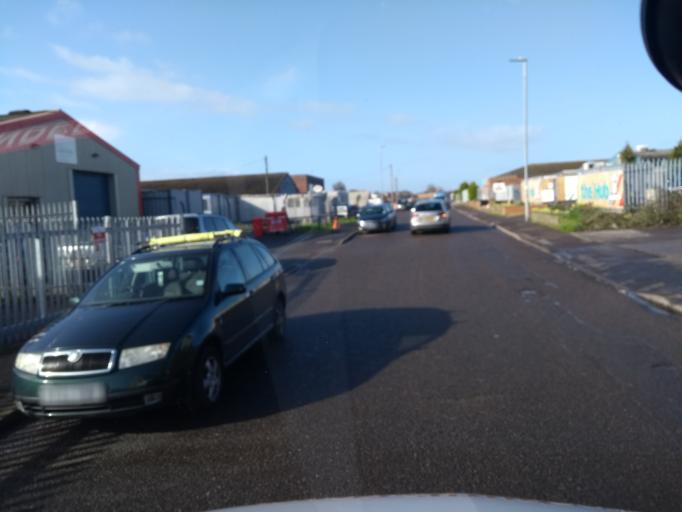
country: GB
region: England
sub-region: Somerset
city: Yeovil
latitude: 50.9475
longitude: -2.6079
